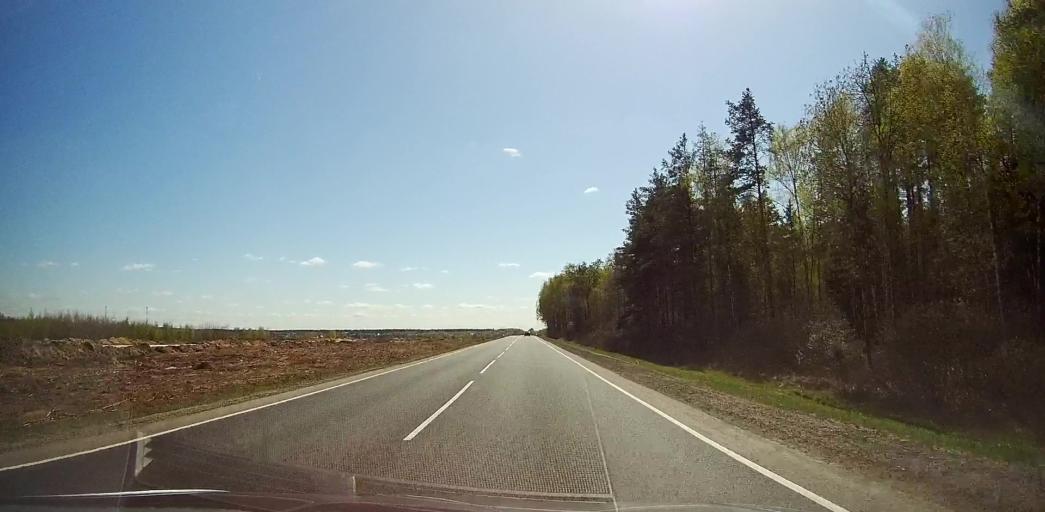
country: RU
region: Moskovskaya
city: Gzhel'
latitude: 55.5875
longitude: 38.3843
